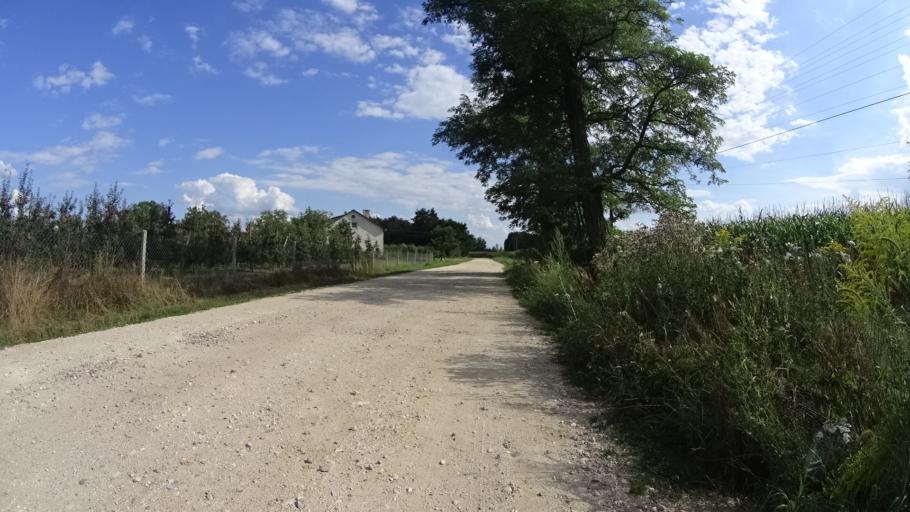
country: PL
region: Masovian Voivodeship
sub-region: Powiat grojecki
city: Mogielnica
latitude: 51.6794
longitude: 20.7645
